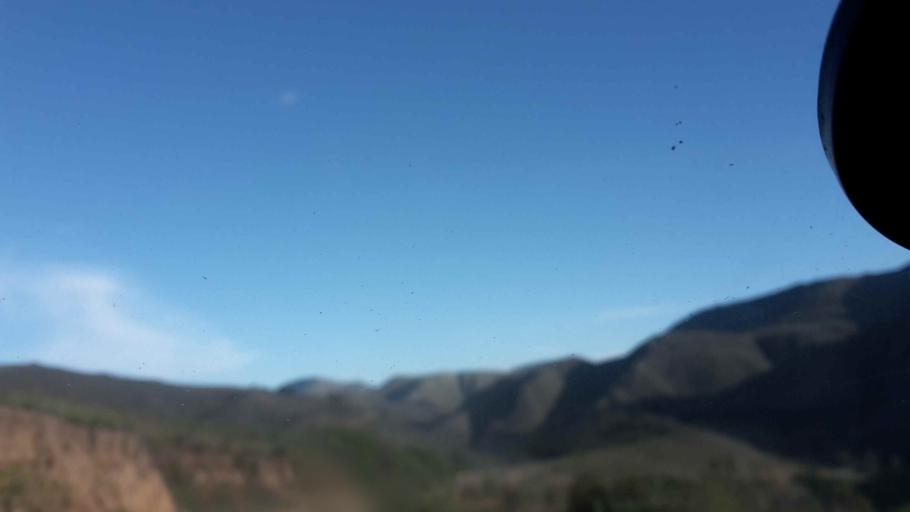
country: BO
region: Cochabamba
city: Arani
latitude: -17.7898
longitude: -65.6016
